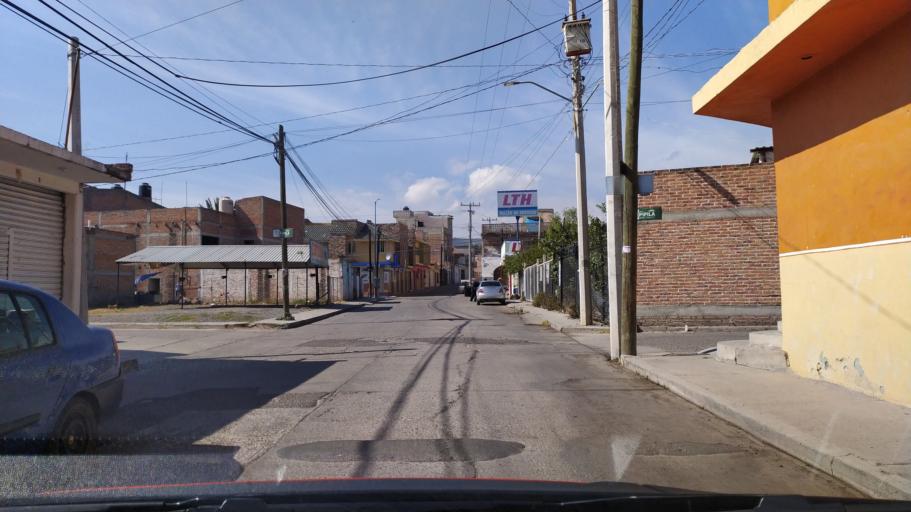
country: MX
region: Guanajuato
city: Ciudad Manuel Doblado
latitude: 20.7321
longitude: -101.9531
